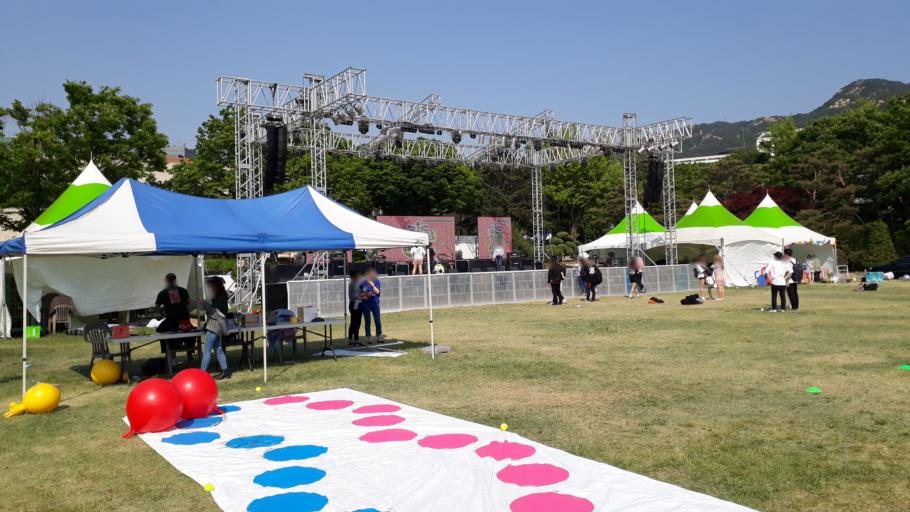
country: KR
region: Gyeonggi-do
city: Anyang-si
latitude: 37.4608
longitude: 126.9506
